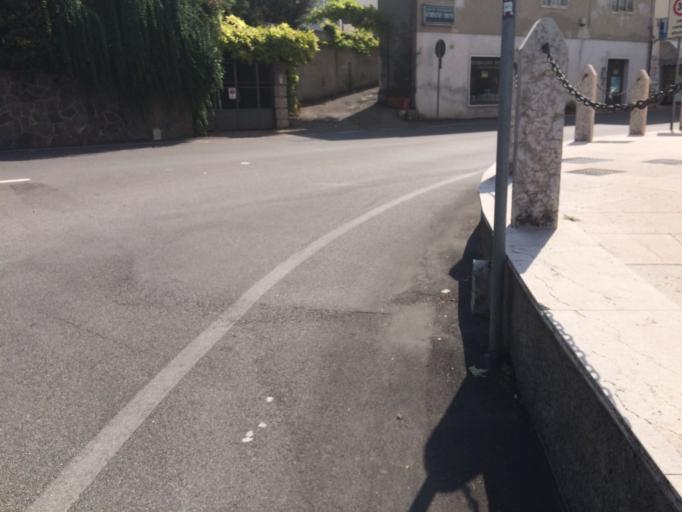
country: IT
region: Veneto
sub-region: Provincia di Verona
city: Volargne
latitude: 45.5220
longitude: 10.8063
